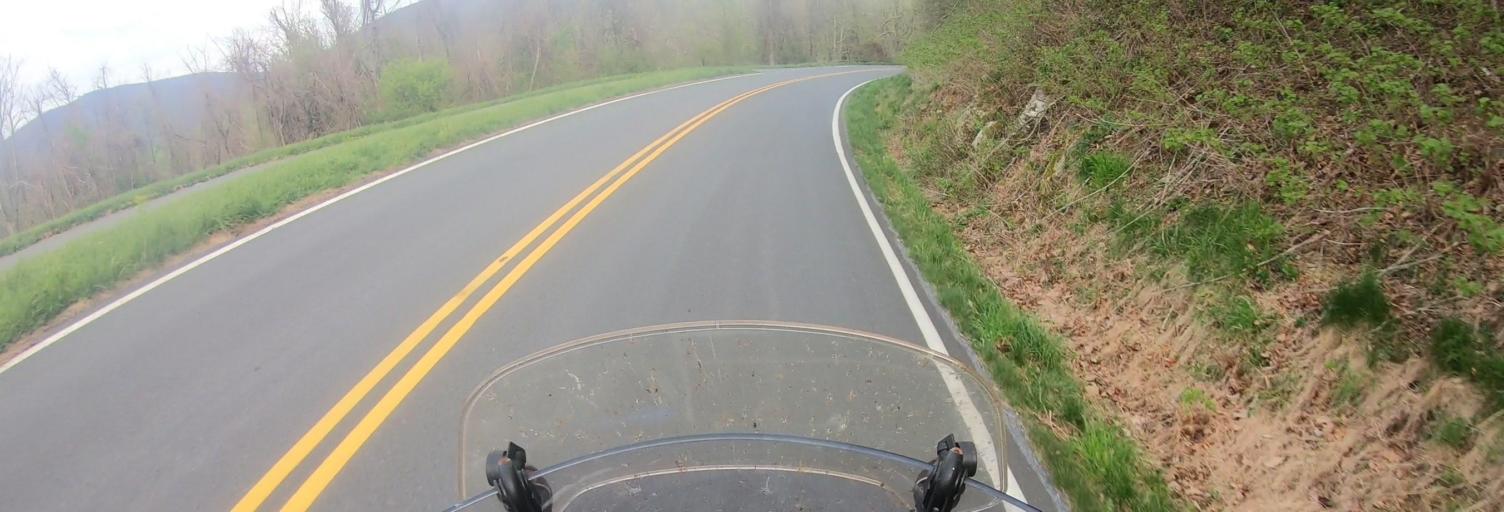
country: US
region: Virginia
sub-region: Augusta County
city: Dooms
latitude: 38.0616
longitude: -78.8216
